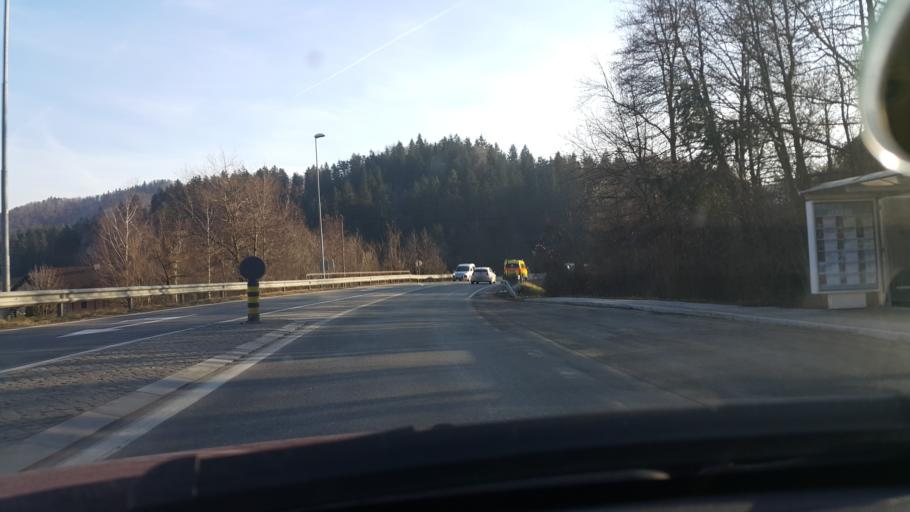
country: SI
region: Dobrna
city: Dobrna
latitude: 46.3410
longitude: 15.1724
